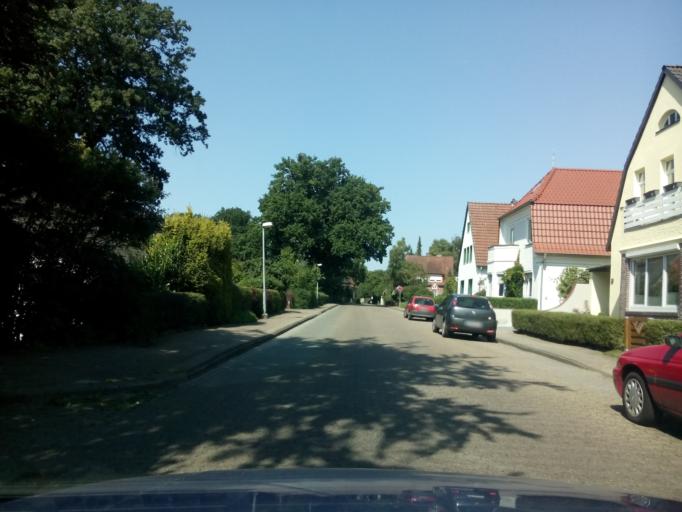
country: DE
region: Lower Saxony
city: Osterholz-Scharmbeck
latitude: 53.2303
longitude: 8.7893
